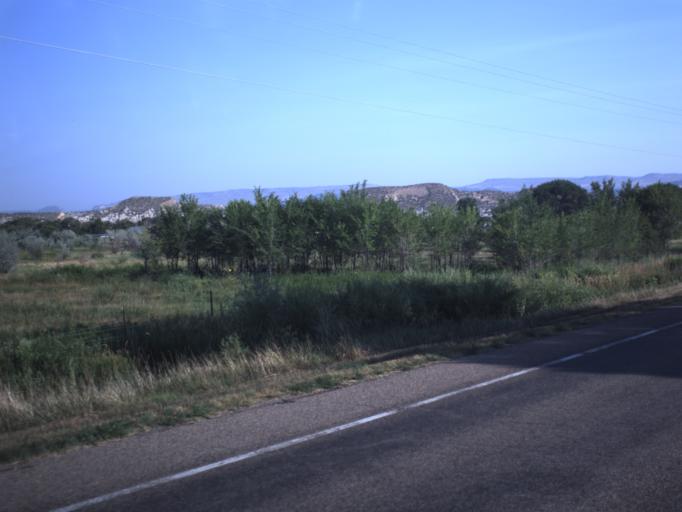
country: US
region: Utah
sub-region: Uintah County
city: Vernal
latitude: 40.4828
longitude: -109.5290
